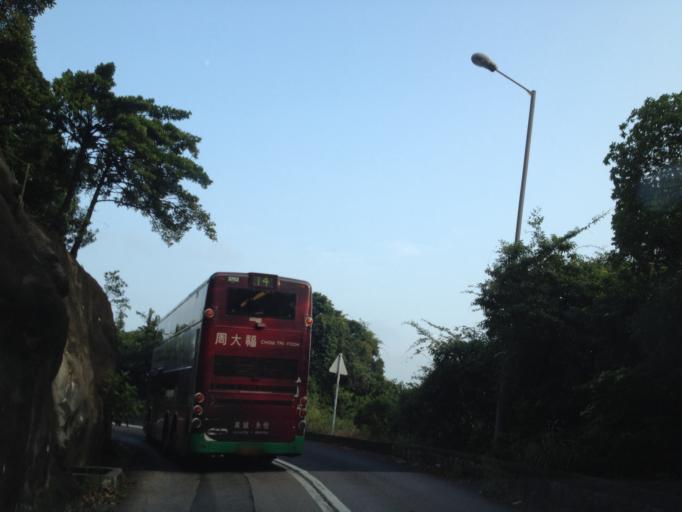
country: HK
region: Wanchai
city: Wan Chai
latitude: 22.2511
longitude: 114.2248
